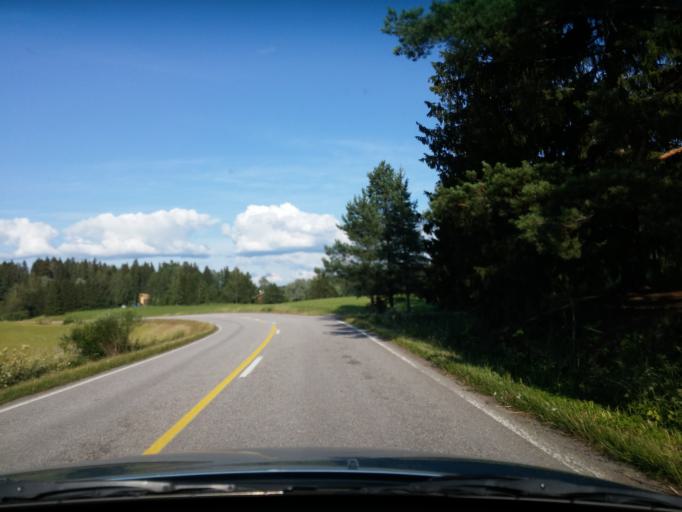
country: FI
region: Uusimaa
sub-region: Porvoo
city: Askola
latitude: 60.5176
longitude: 25.5305
